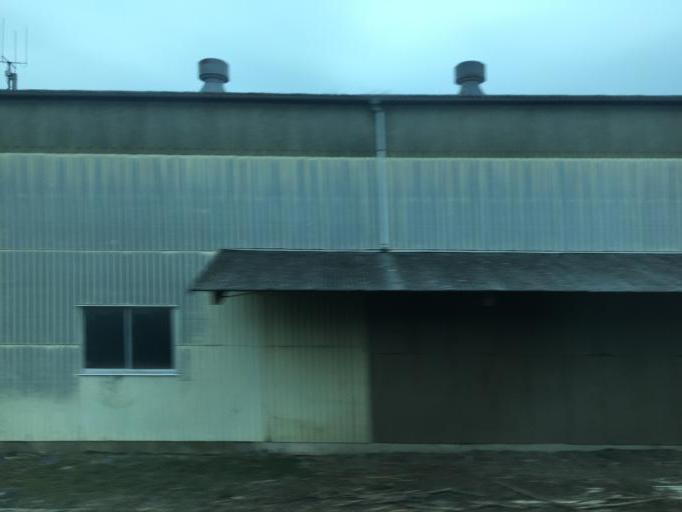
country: JP
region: Ibaraki
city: Yuki
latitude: 36.2970
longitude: 139.8827
